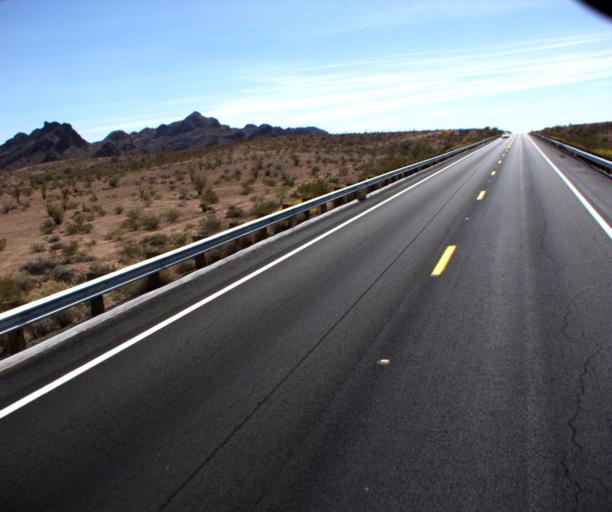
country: US
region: Arizona
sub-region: La Paz County
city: Quartzsite
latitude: 33.2492
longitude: -114.2473
